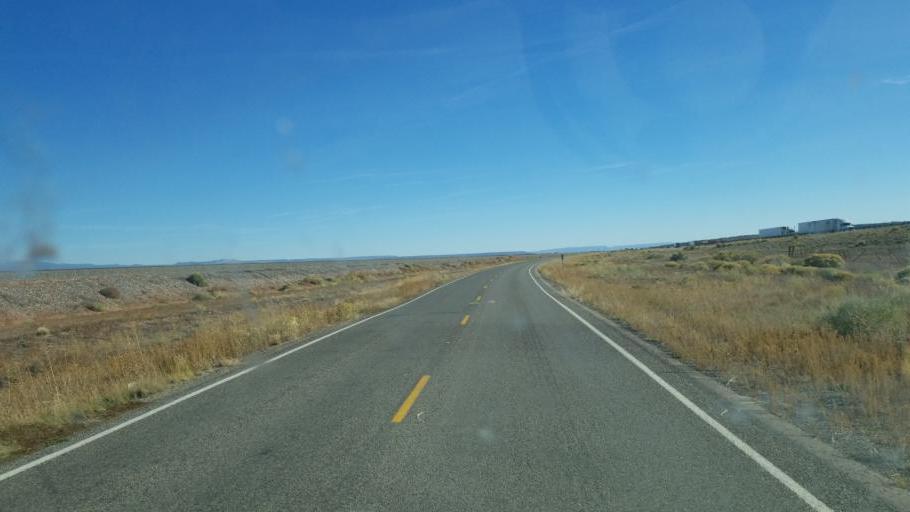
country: US
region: New Mexico
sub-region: Cibola County
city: Milan
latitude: 35.3461
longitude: -108.0095
